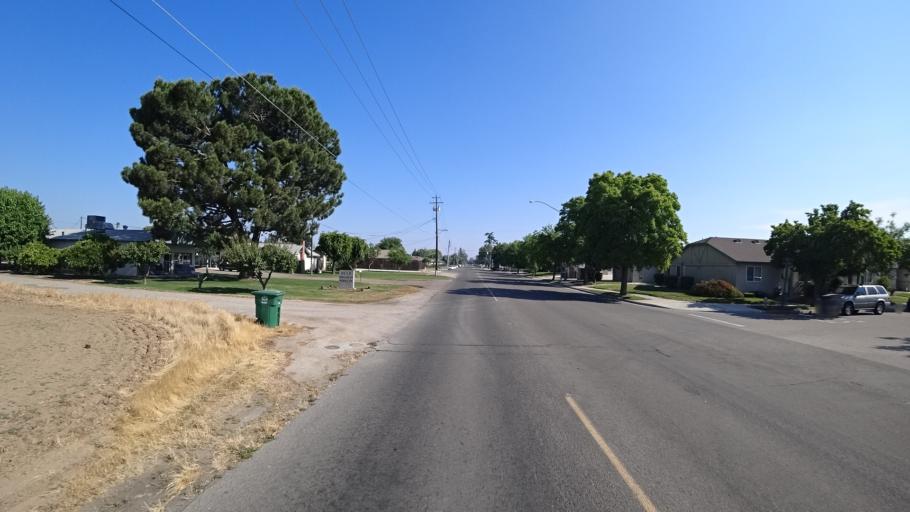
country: US
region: California
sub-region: Fresno County
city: Kingsburg
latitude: 36.5061
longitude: -119.5569
